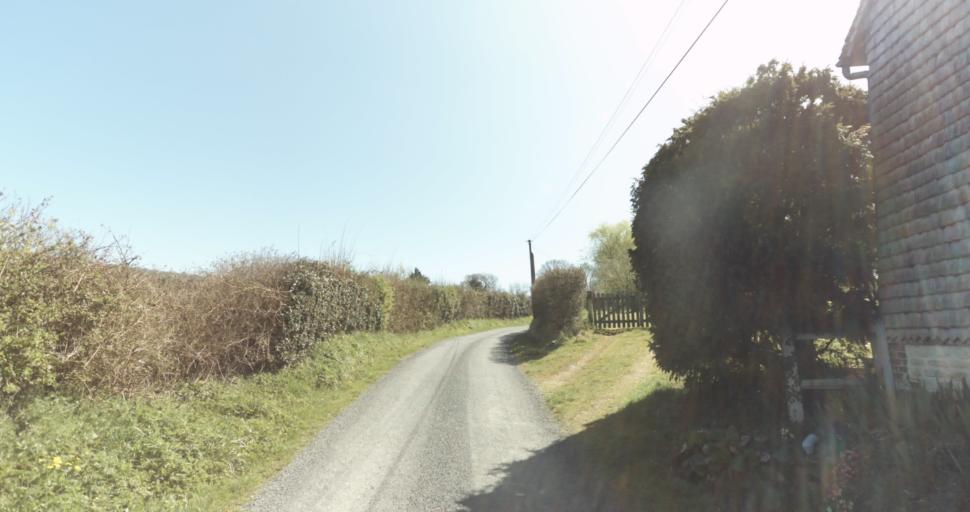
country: FR
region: Lower Normandy
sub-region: Departement du Calvados
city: Saint-Pierre-sur-Dives
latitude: 49.0051
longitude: 0.0320
